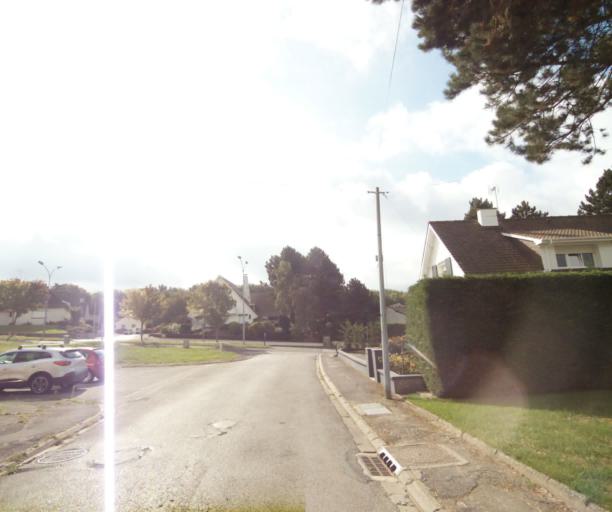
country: FR
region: Nord-Pas-de-Calais
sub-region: Departement du Pas-de-Calais
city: Etaples
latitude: 50.5264
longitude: 1.6328
